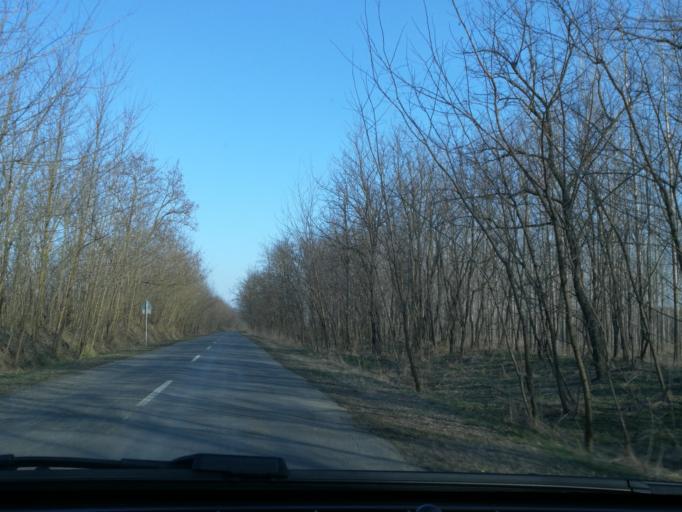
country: HU
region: Szabolcs-Szatmar-Bereg
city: Nyirbogdany
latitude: 48.0211
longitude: 21.9209
